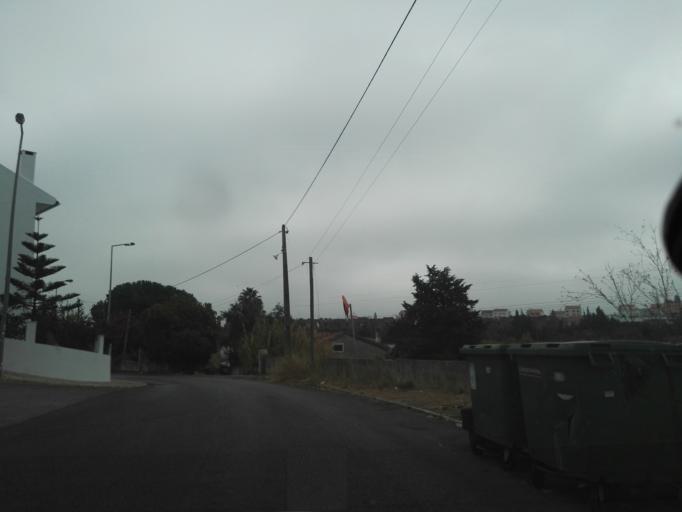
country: PT
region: Lisbon
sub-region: Vila Franca de Xira
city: Sobralinho
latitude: 38.8993
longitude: -9.0481
